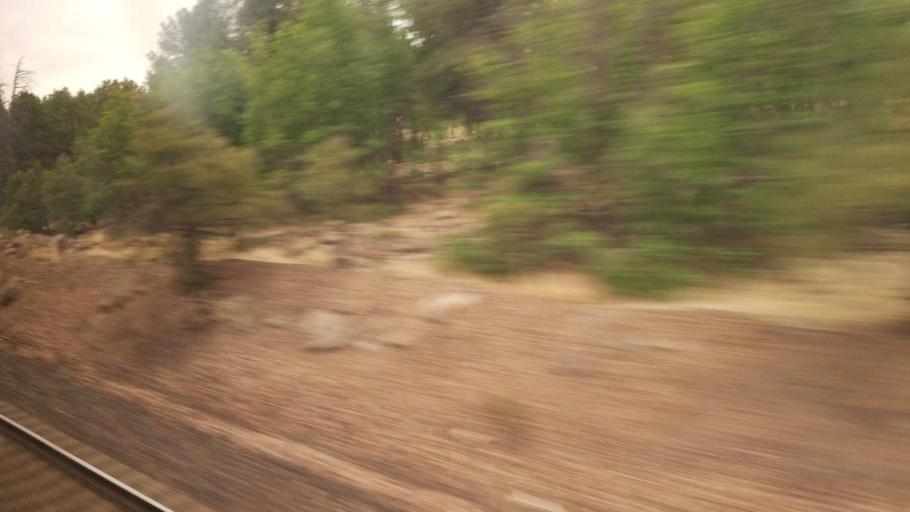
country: US
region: Arizona
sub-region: Coconino County
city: Parks
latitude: 35.2320
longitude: -112.0214
